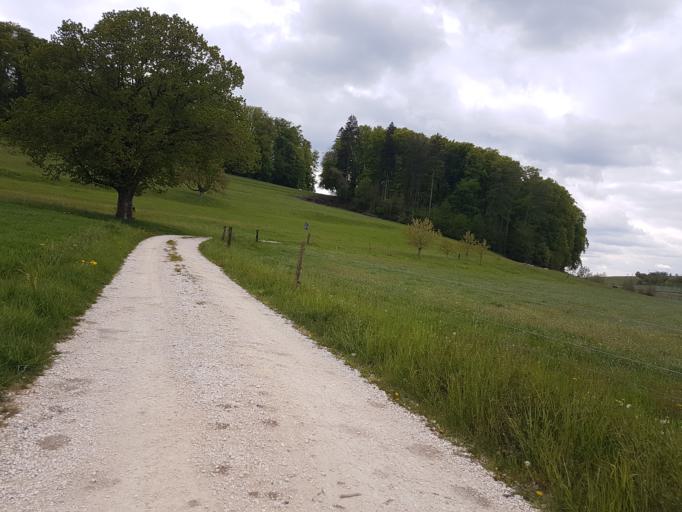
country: CH
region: Bern
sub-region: Seeland District
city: Leuzigen
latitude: 47.1799
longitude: 7.4804
